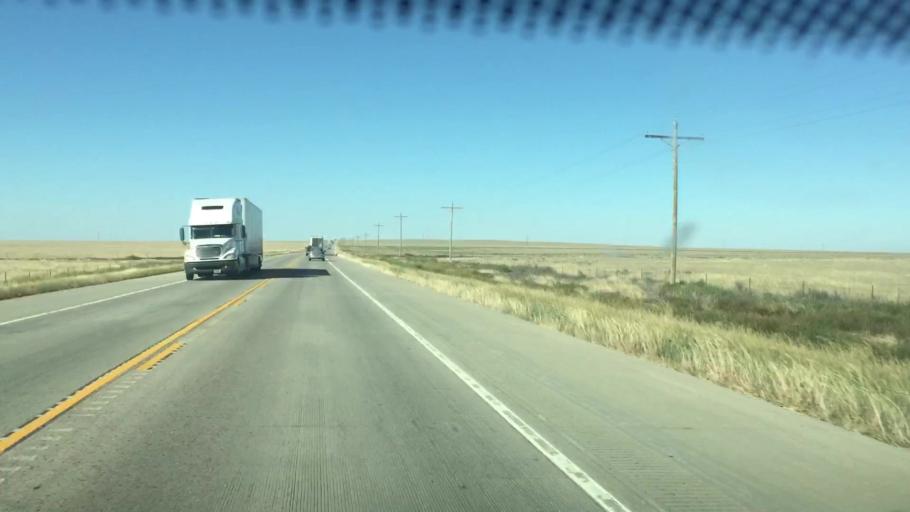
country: US
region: Colorado
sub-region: Prowers County
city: Lamar
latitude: 38.2433
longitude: -102.7240
